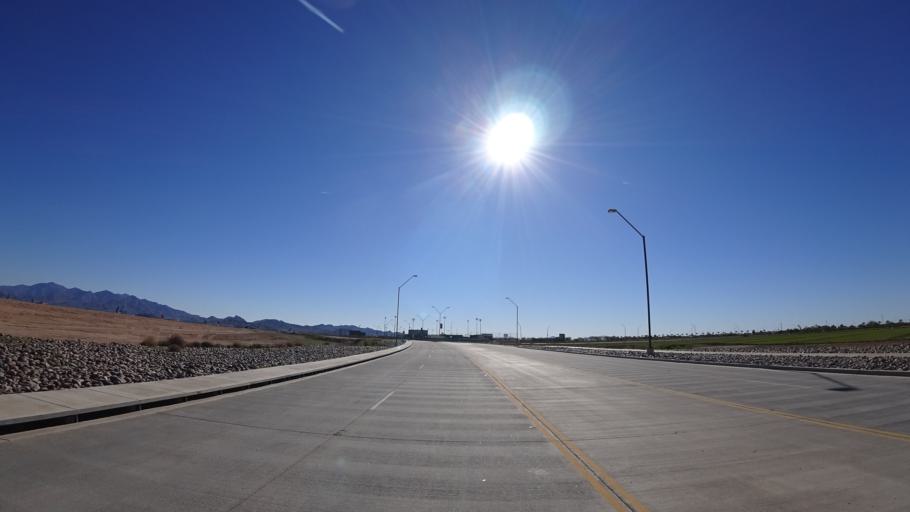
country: US
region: Arizona
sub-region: Maricopa County
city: Goodyear
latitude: 33.4276
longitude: -112.3833
